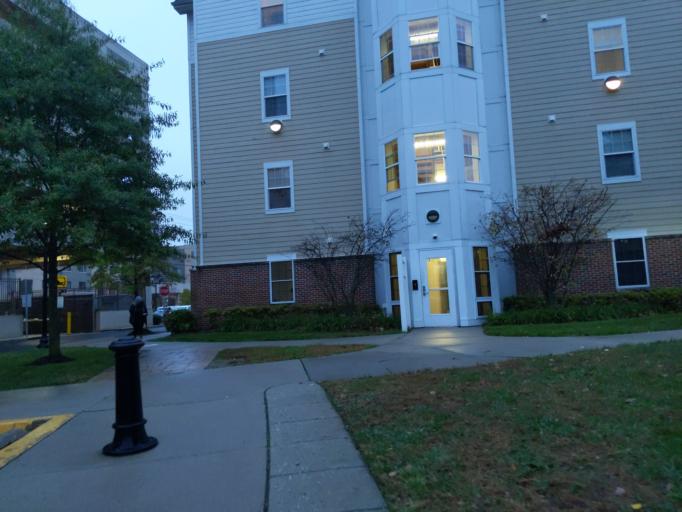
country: US
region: New Jersey
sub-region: Gloucester County
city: Glassboro
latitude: 39.7060
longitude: -75.1124
